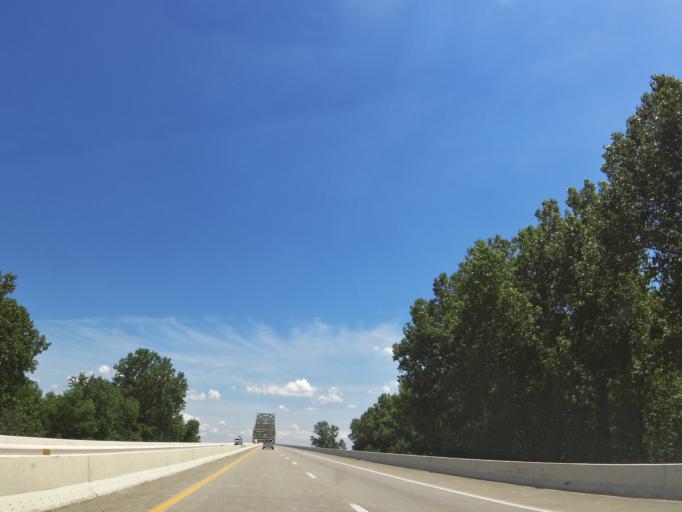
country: US
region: Missouri
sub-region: Pemiscot County
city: Caruthersville
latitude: 36.1204
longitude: -89.6162
